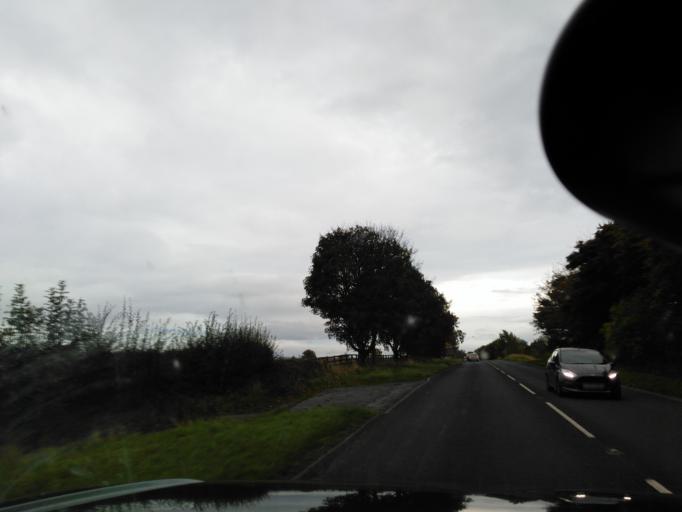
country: GB
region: England
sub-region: North Yorkshire
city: Northallerton
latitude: 54.3241
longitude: -1.4706
